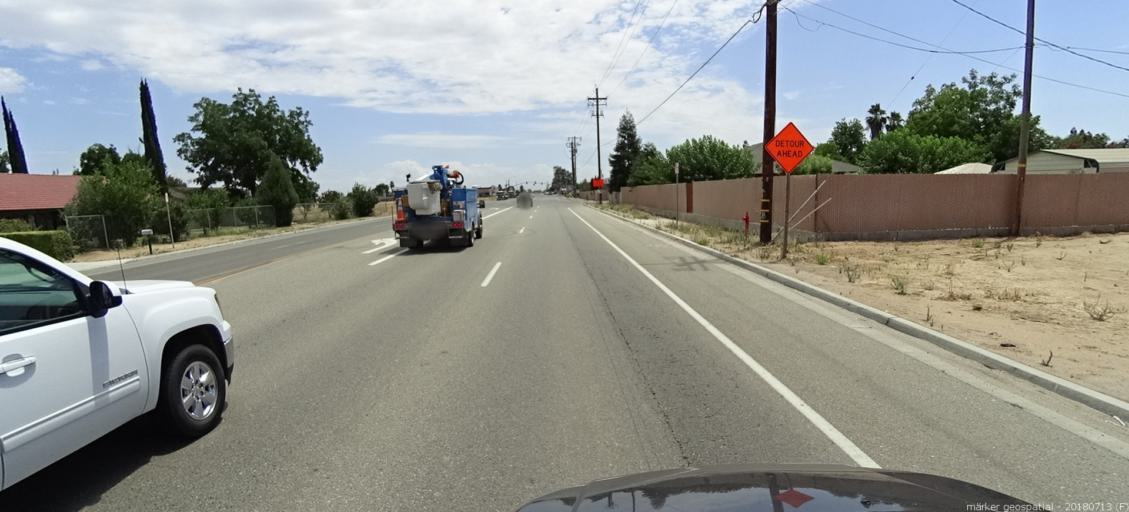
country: US
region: California
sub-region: Madera County
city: Madera Acres
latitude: 36.9963
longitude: -120.0777
